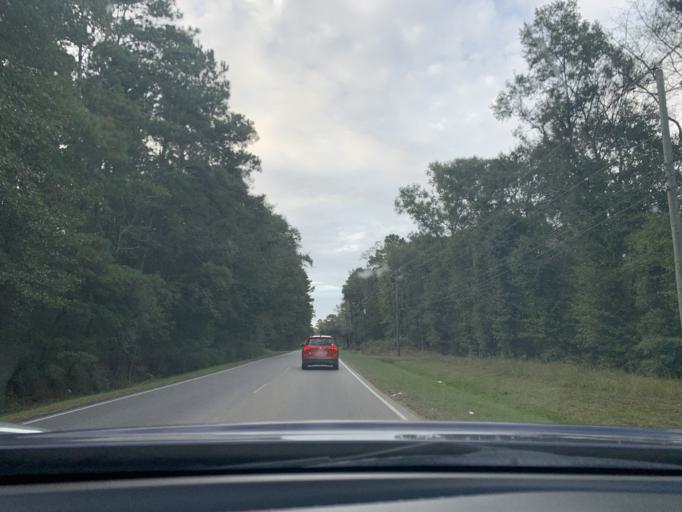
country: US
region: Georgia
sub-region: Chatham County
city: Pooler
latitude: 32.0472
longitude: -81.2640
